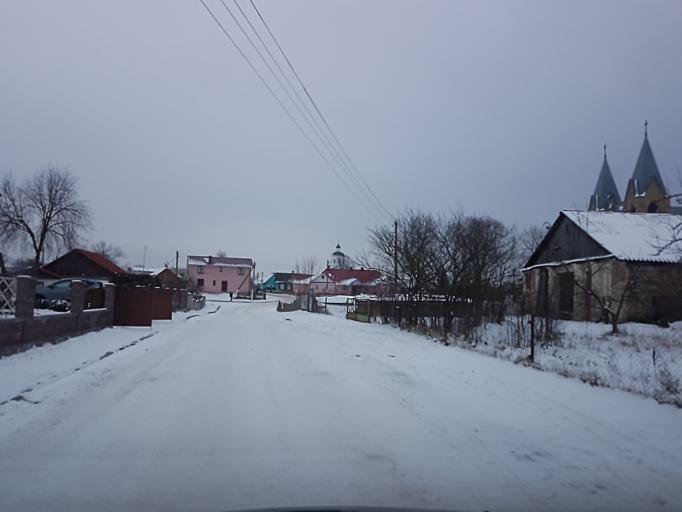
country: BY
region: Minsk
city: Rakaw
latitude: 53.9658
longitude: 27.0539
